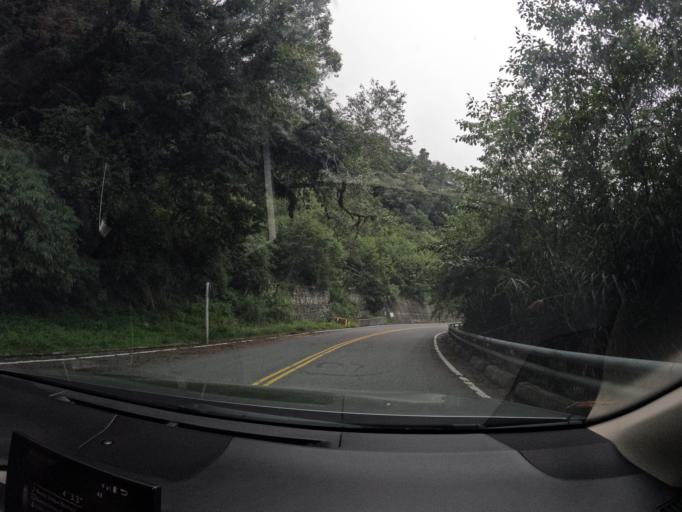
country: TW
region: Taiwan
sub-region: Taitung
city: Taitung
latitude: 23.2461
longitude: 120.9936
